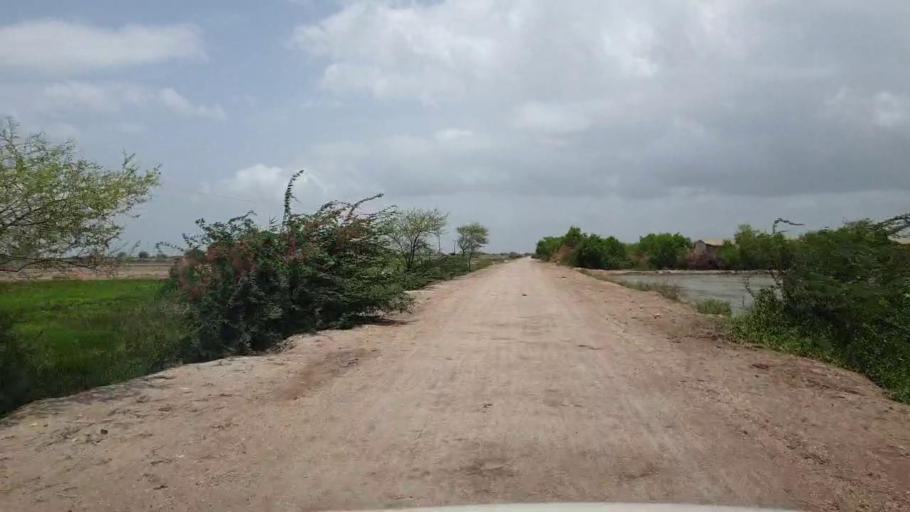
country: PK
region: Sindh
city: Kario
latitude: 24.6979
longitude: 68.6377
